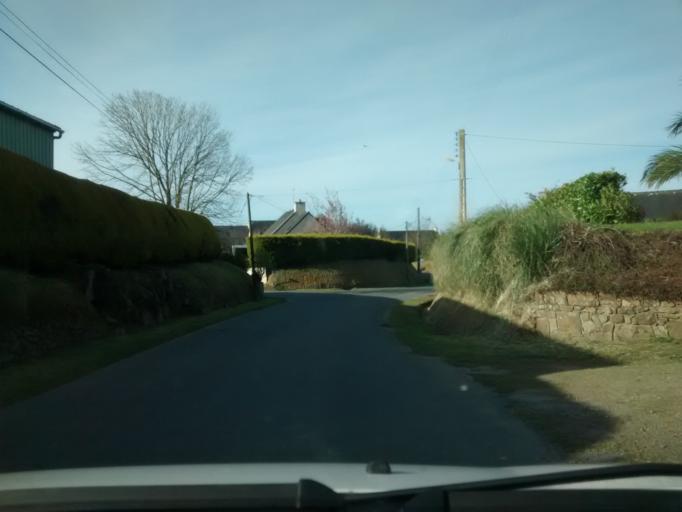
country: FR
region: Brittany
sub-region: Departement des Cotes-d'Armor
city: Penvenan
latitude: 48.7805
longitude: -3.3034
